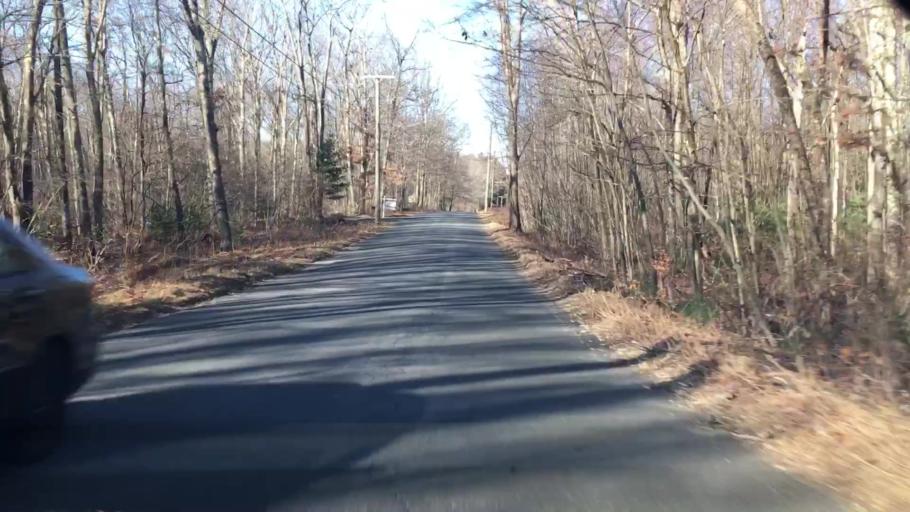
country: US
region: Connecticut
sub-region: Tolland County
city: Crystal Lake
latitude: 41.9582
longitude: -72.4052
